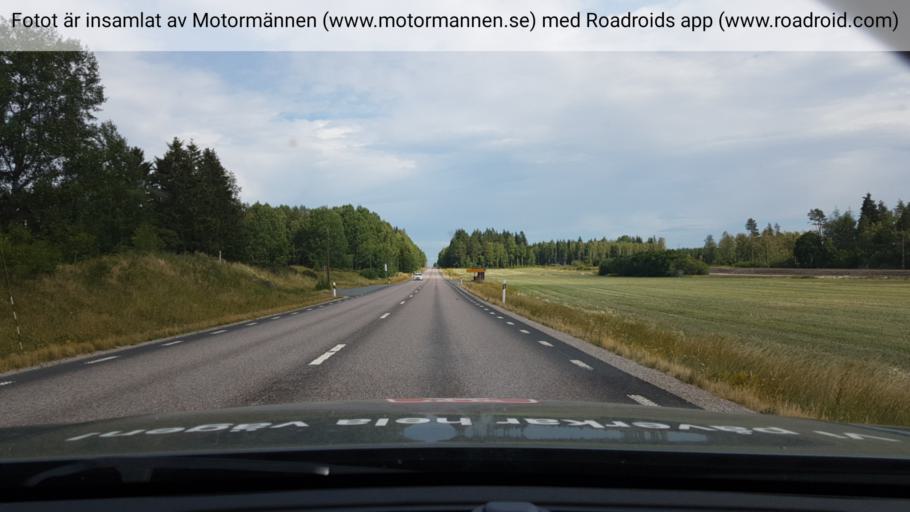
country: SE
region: Uppsala
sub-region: Enkopings Kommun
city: Orsundsbro
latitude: 59.8700
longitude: 17.3117
